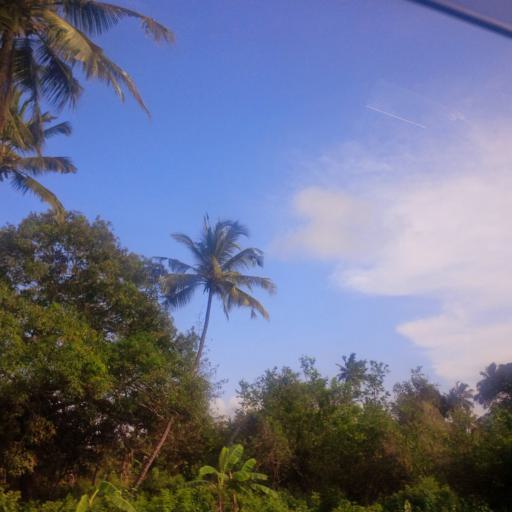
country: TZ
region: Zanzibar Central/South
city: Nganane
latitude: -6.2898
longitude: 39.4389
